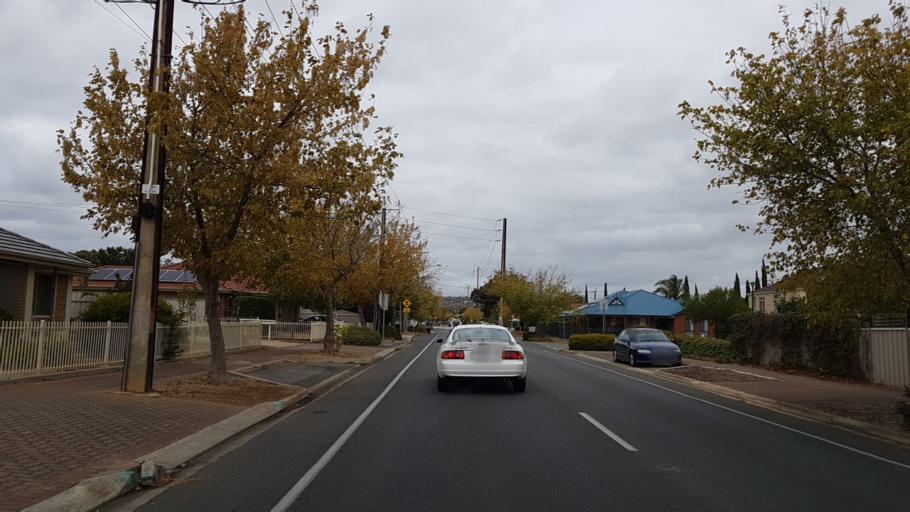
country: AU
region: South Australia
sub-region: Marion
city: Clovelly Park
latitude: -35.0069
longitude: 138.5658
